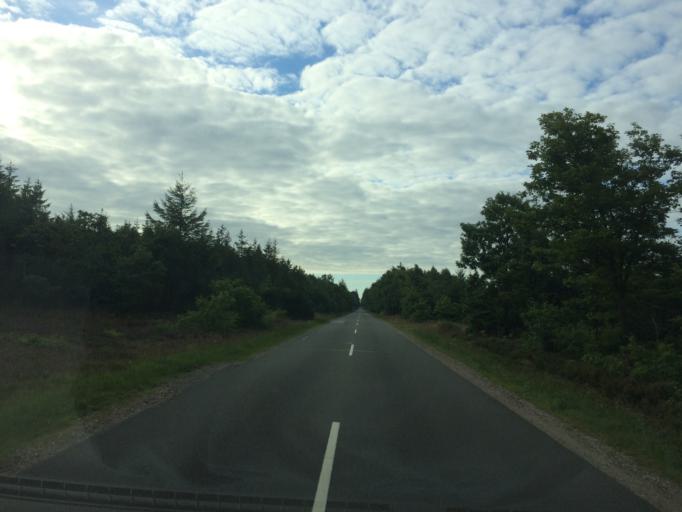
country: DK
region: Central Jutland
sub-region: Holstebro Kommune
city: Ulfborg
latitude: 56.2150
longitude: 8.3927
